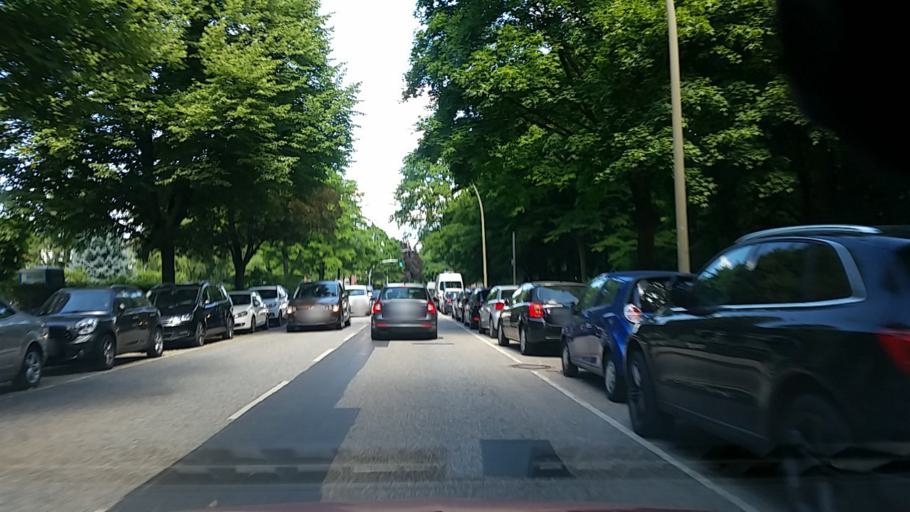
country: DE
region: Hamburg
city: Winterhude
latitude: 53.5973
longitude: 10.0033
